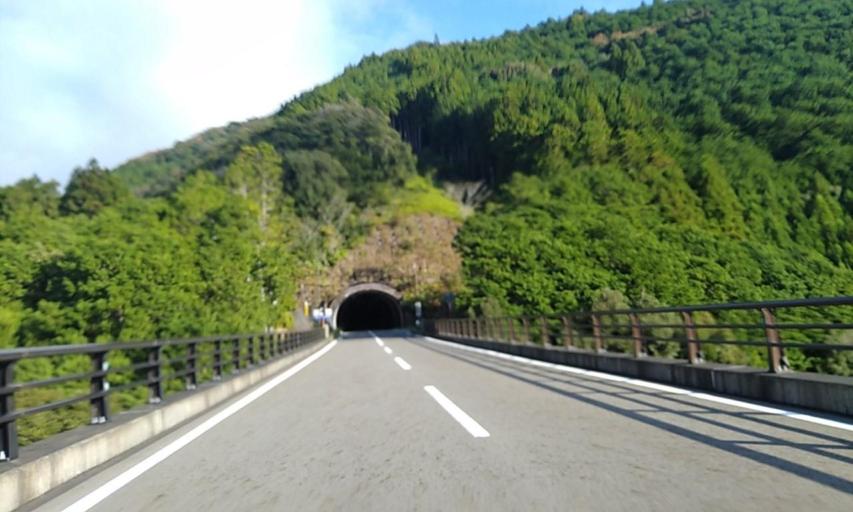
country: JP
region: Wakayama
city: Shingu
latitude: 33.8946
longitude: 135.8796
